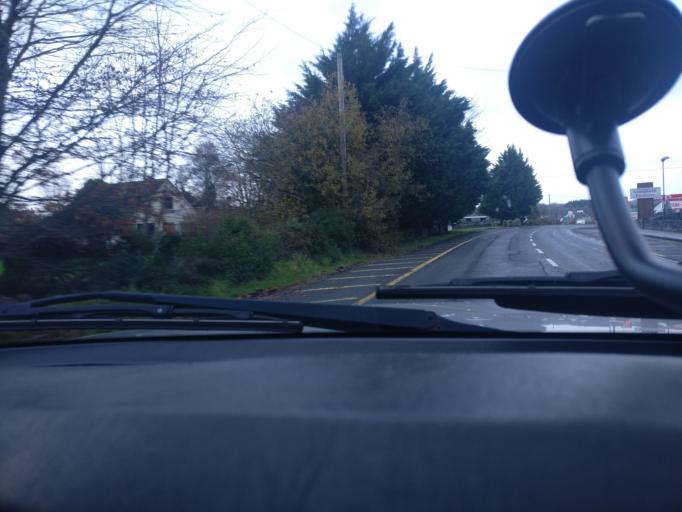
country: IE
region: Connaught
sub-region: County Galway
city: Athenry
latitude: 53.2261
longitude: -8.7297
